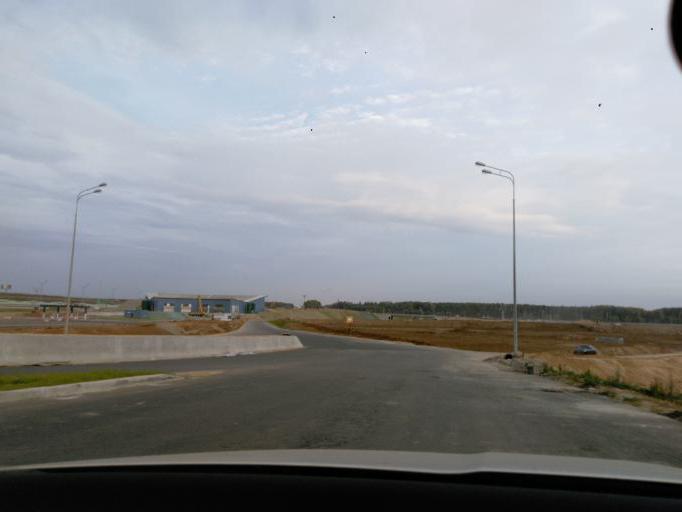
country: RU
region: Moskovskaya
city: Novopodrezkovo
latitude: 55.9593
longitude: 37.3684
